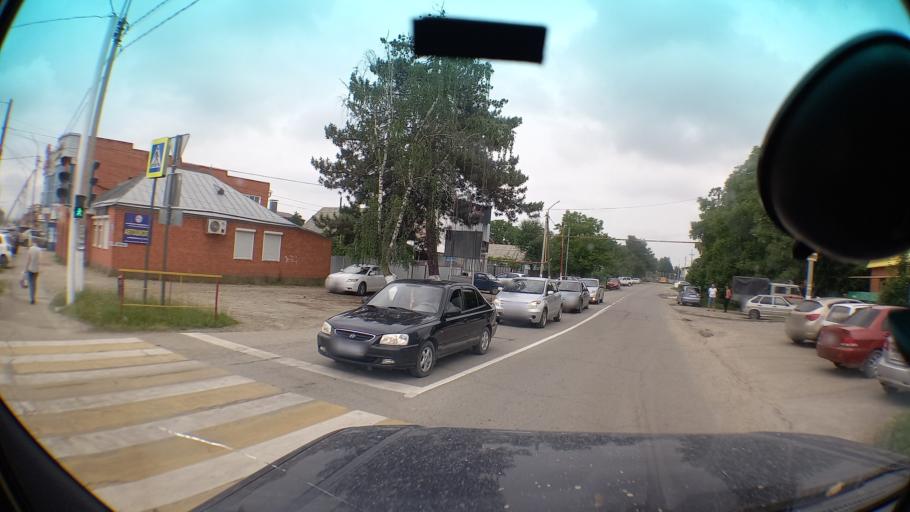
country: RU
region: Krasnodarskiy
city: Mostovskoy
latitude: 44.4088
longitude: 40.8032
